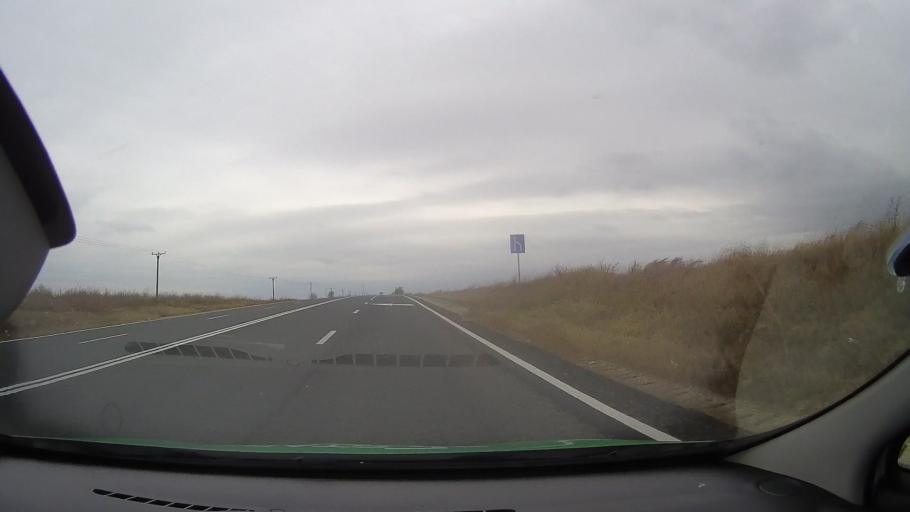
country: RO
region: Constanta
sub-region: Comuna Nicolae Balcescu
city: Nicolae Balcescu
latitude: 44.3804
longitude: 28.4077
